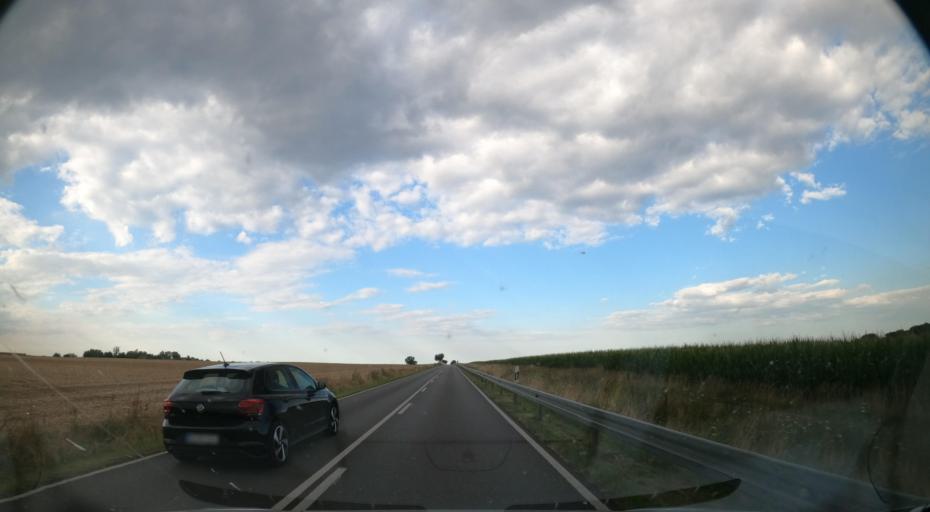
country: DE
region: Mecklenburg-Vorpommern
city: Pasewalk
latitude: 53.5033
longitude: 13.9569
